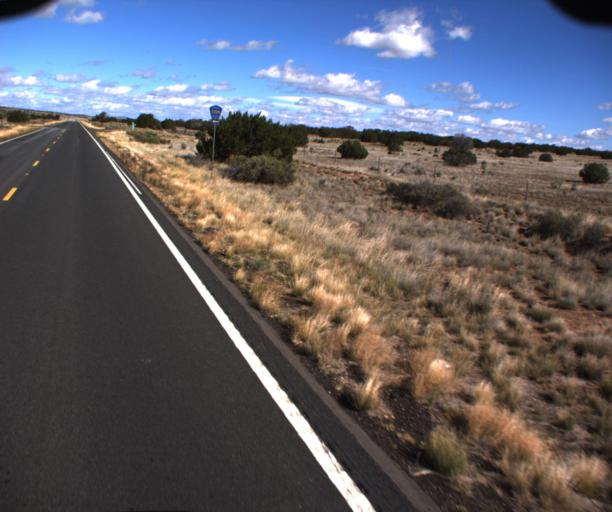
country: US
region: Arizona
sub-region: Apache County
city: Houck
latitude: 34.9062
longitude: -109.2381
